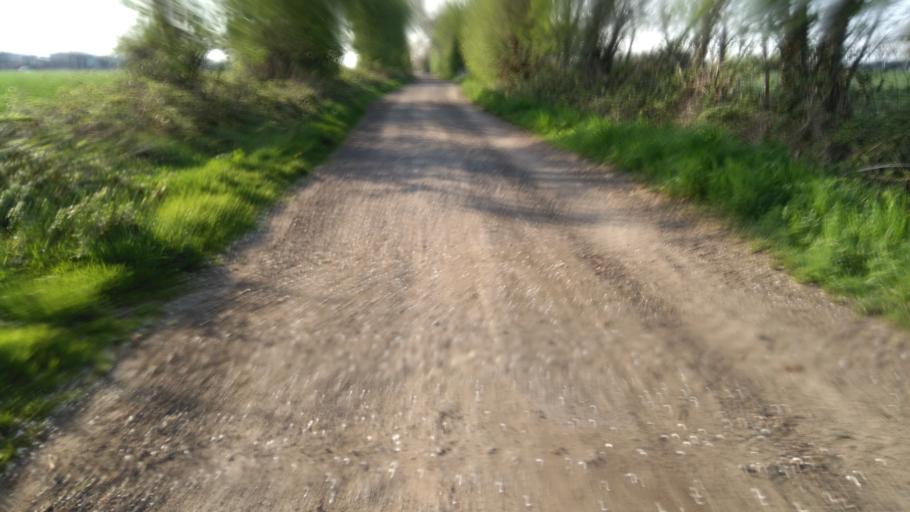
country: DE
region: Lower Saxony
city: Apensen
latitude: 53.4415
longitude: 9.6346
